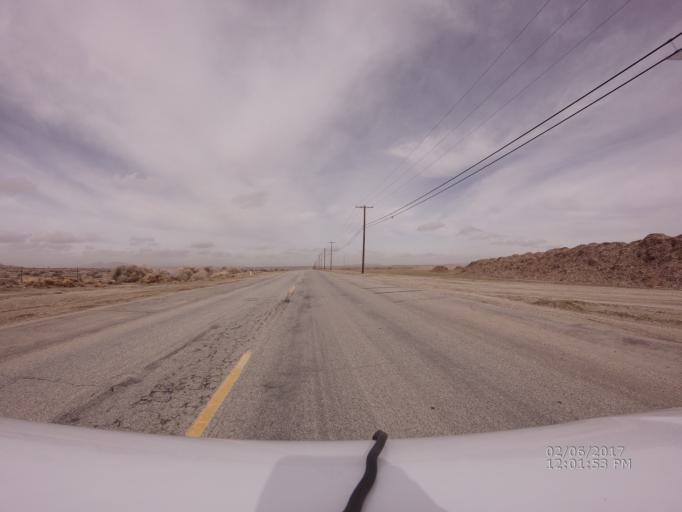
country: US
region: California
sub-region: Los Angeles County
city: Lake Los Angeles
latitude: 34.5701
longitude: -117.7026
